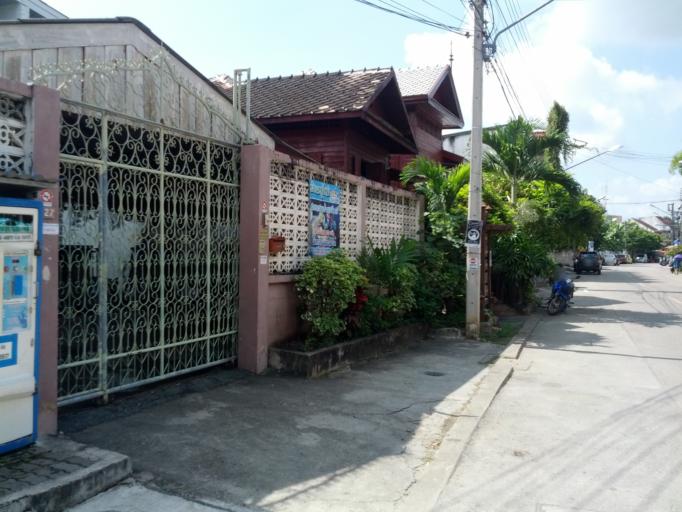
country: TH
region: Lampang
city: Lampang
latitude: 18.2909
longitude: 99.4982
